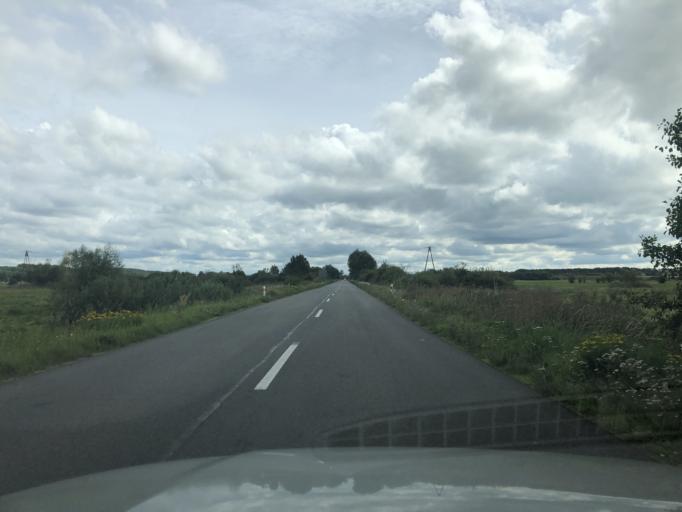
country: PL
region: Lubusz
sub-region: Powiat strzelecko-drezdenecki
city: Drezdenko
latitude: 52.8466
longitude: 15.8467
